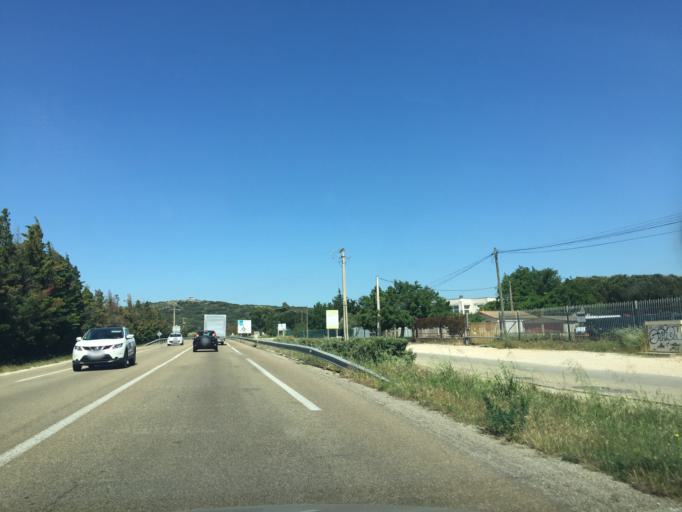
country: FR
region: Languedoc-Roussillon
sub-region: Departement du Gard
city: Saze
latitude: 43.9546
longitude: 4.6590
